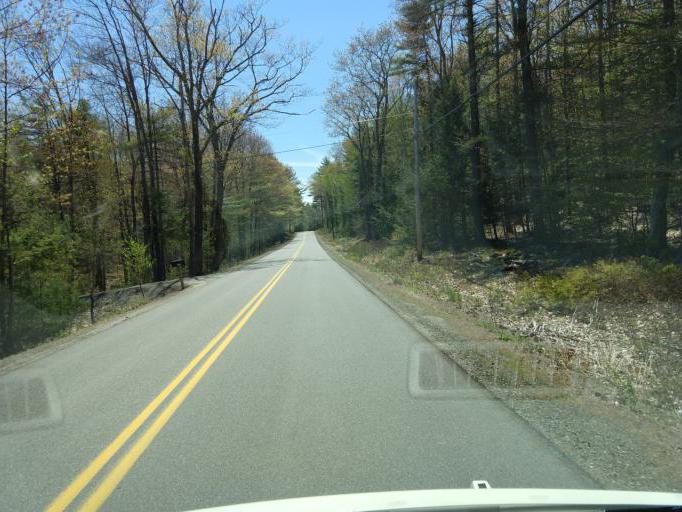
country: US
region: Maine
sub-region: York County
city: Ogunquit
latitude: 43.2333
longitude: -70.6212
